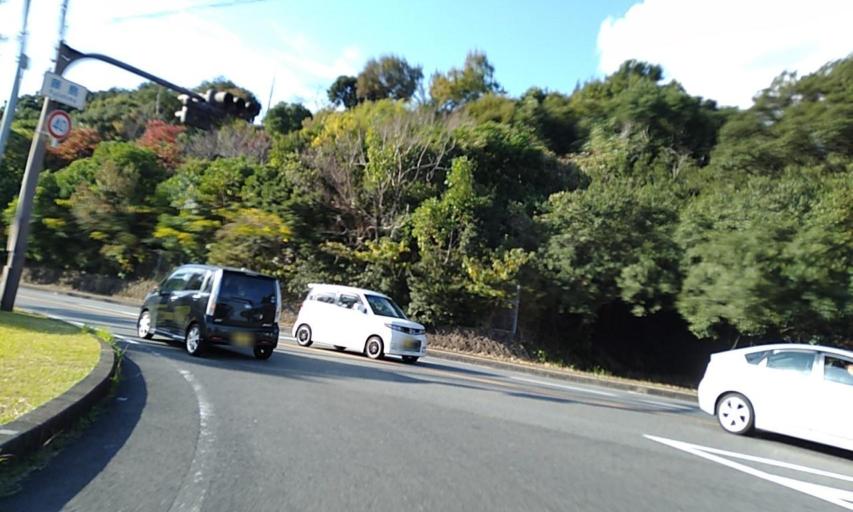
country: JP
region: Wakayama
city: Tanabe
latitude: 33.6795
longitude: 135.3709
